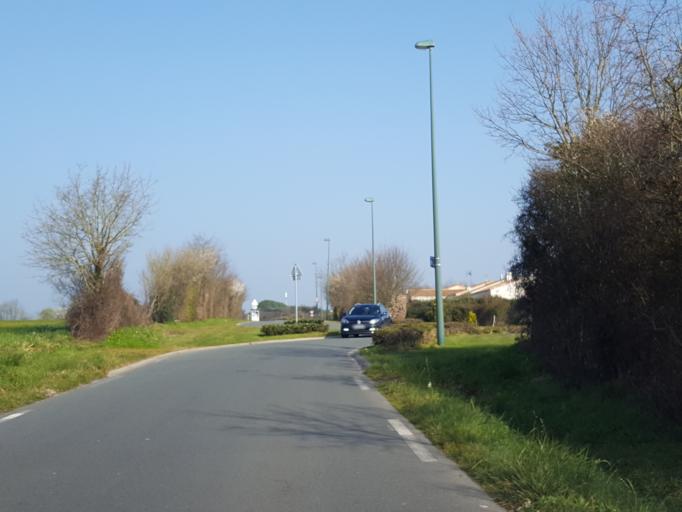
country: FR
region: Pays de la Loire
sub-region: Departement de la Vendee
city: La Roche-sur-Yon
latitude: 46.6763
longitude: -1.4508
